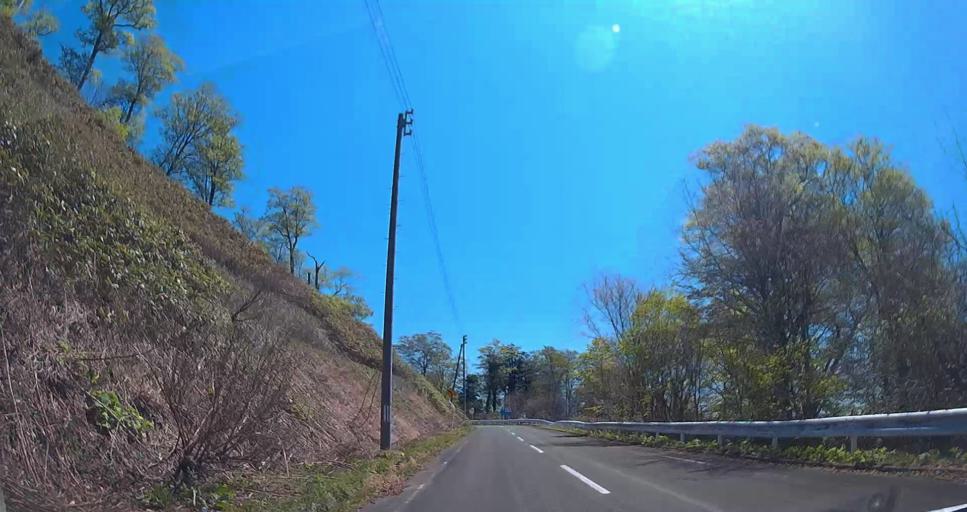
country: JP
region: Aomori
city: Mutsu
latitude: 41.2310
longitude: 140.8151
